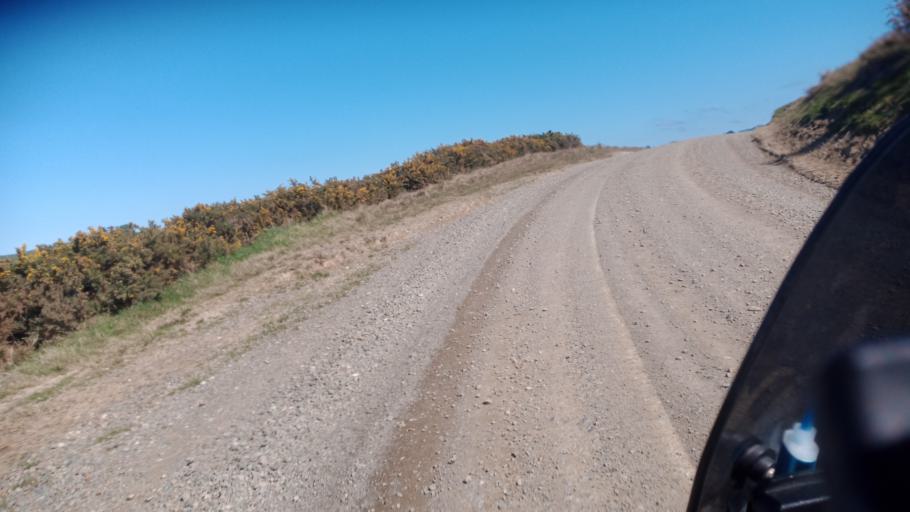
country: NZ
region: Gisborne
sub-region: Gisborne District
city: Gisborne
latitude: -39.1048
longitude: 177.9629
